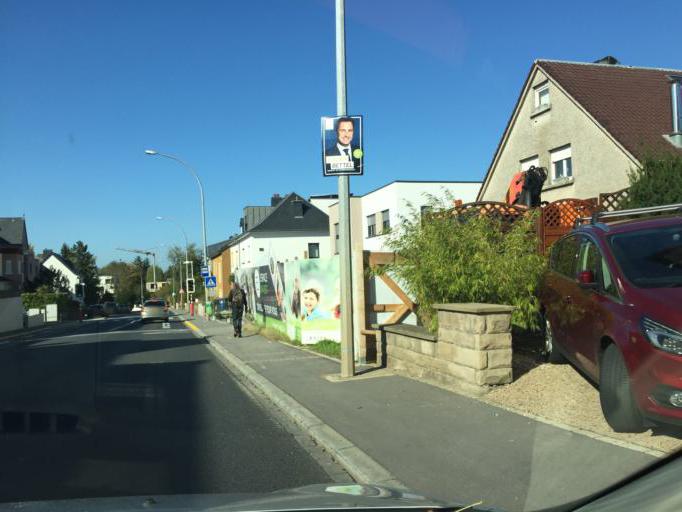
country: LU
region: Luxembourg
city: Bridel
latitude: 49.6587
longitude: 6.0818
